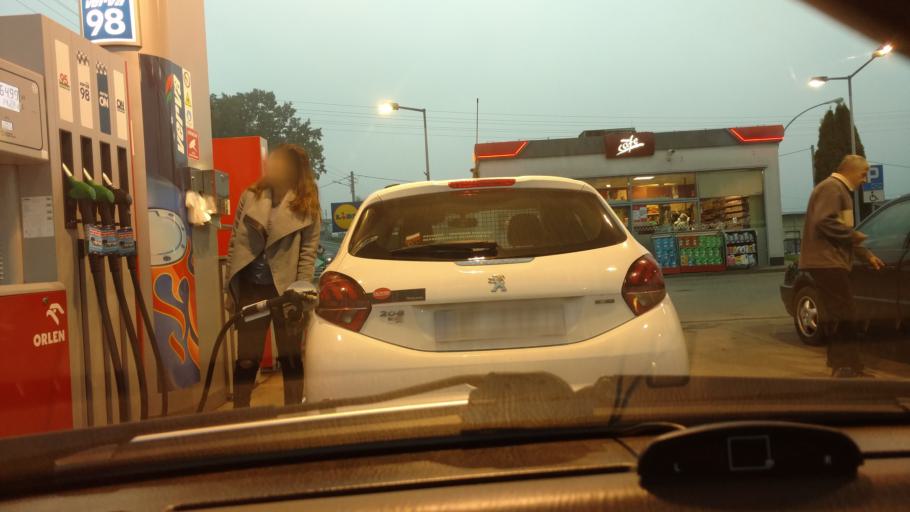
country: PL
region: Subcarpathian Voivodeship
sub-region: Powiat strzyzowski
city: Strzyzow
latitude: 49.8717
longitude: 21.7751
